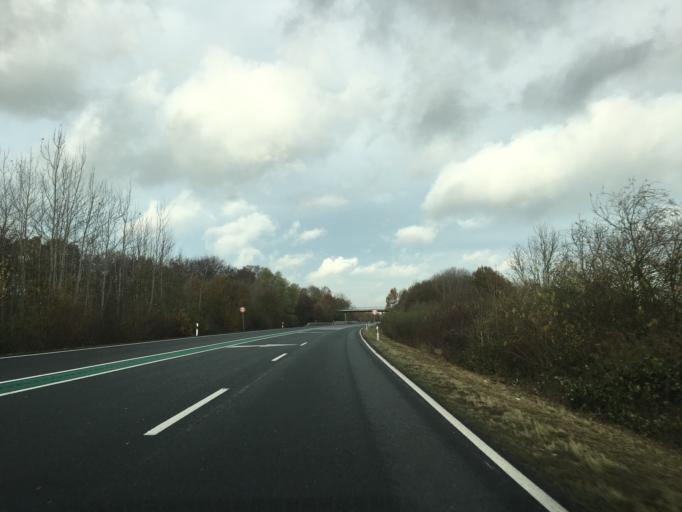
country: DE
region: North Rhine-Westphalia
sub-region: Regierungsbezirk Munster
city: Altenberge
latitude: 52.0806
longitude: 7.4197
